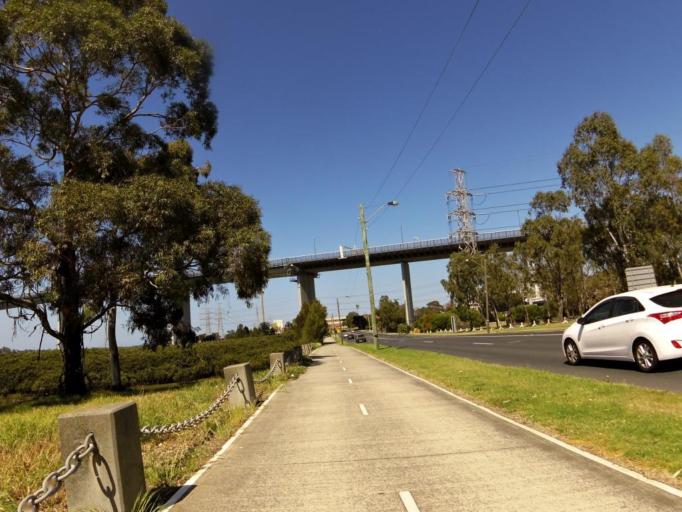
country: AU
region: Victoria
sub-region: Hobsons Bay
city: Spotswood
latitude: -37.8249
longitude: 144.8954
